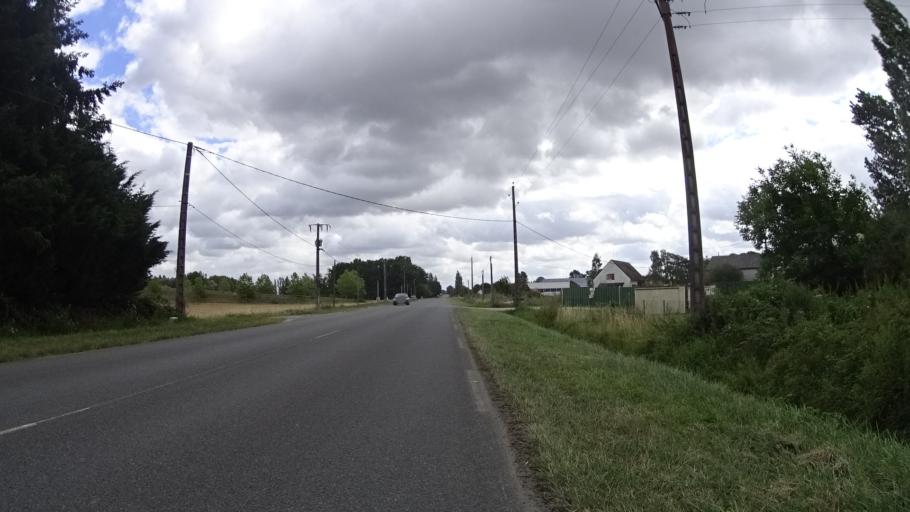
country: FR
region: Centre
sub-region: Departement du Loiret
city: Saint-Maurice-sur-Fessard
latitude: 47.9870
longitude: 2.6536
